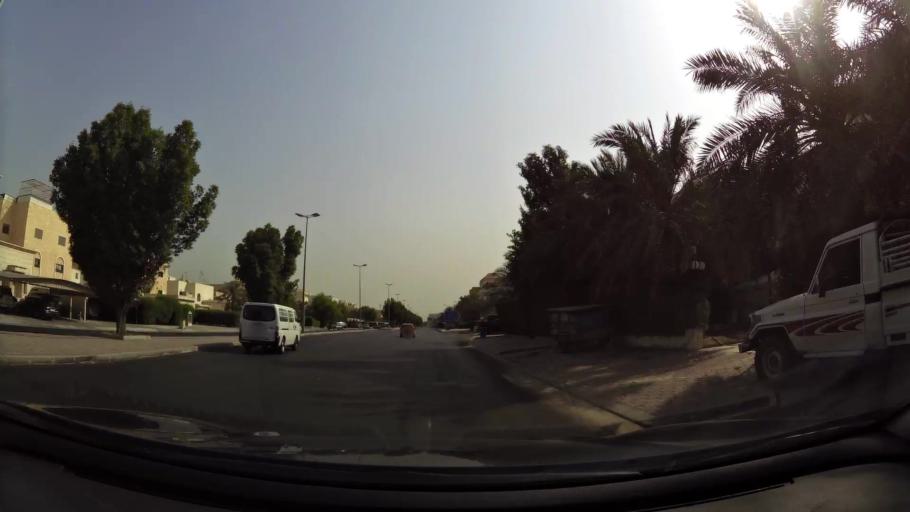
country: KW
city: Bayan
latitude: 29.2819
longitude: 48.0523
